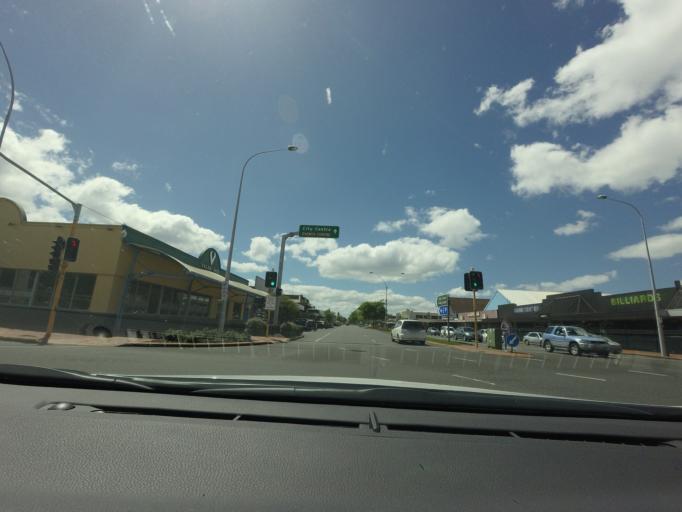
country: NZ
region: Bay of Plenty
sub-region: Rotorua District
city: Rotorua
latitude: -38.1399
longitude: 176.2537
